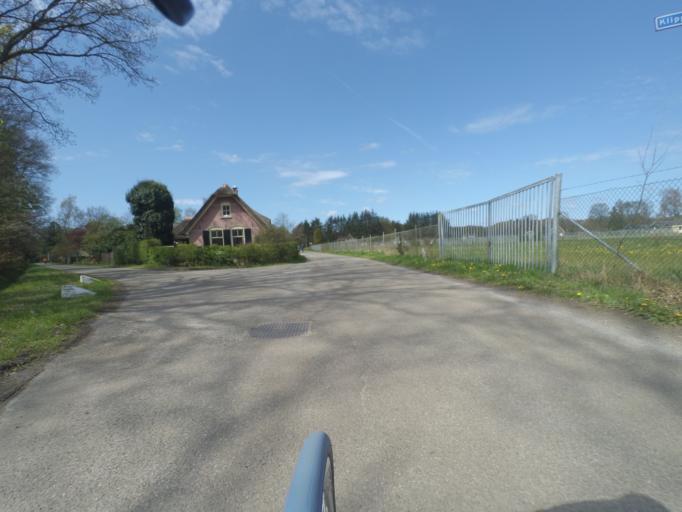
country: NL
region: Gelderland
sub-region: Gemeente Heerde
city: Heerde
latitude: 52.3789
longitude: 6.0091
